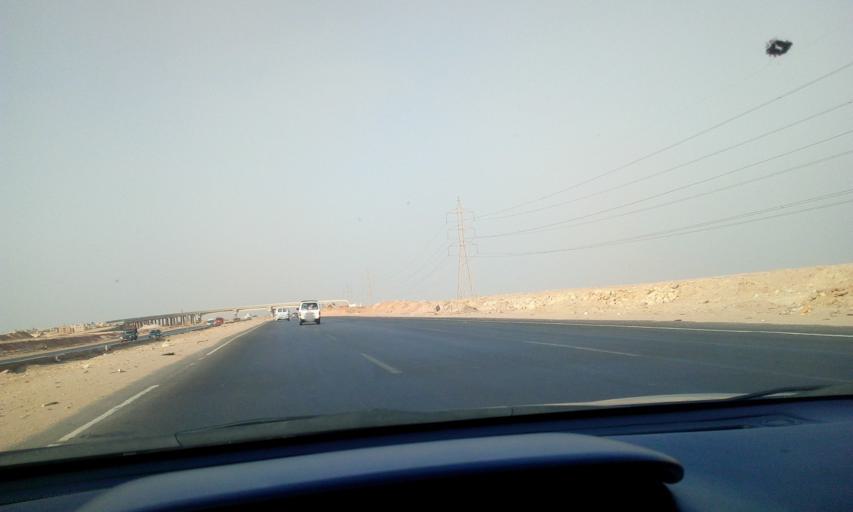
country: EG
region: Al Jizah
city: Madinat Sittah Uktubar
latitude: 29.9056
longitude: 31.0879
